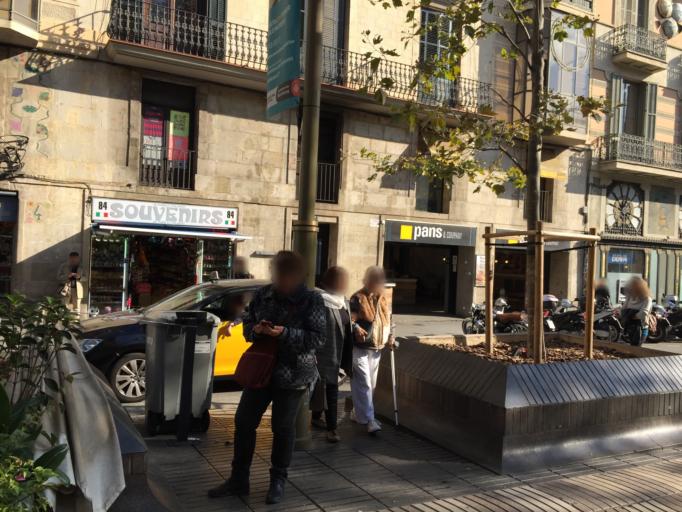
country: ES
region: Catalonia
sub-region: Provincia de Barcelona
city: Ciutat Vella
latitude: 41.3816
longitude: 2.1730
